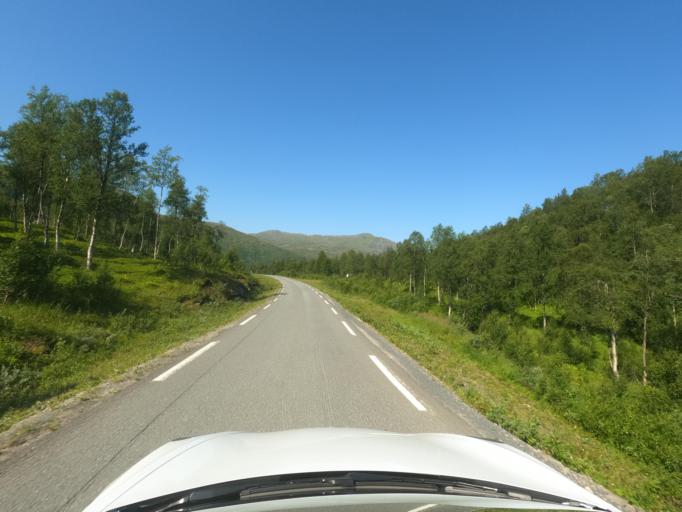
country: NO
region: Troms
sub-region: Skanland
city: Evenskjer
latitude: 68.3283
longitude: 16.5694
